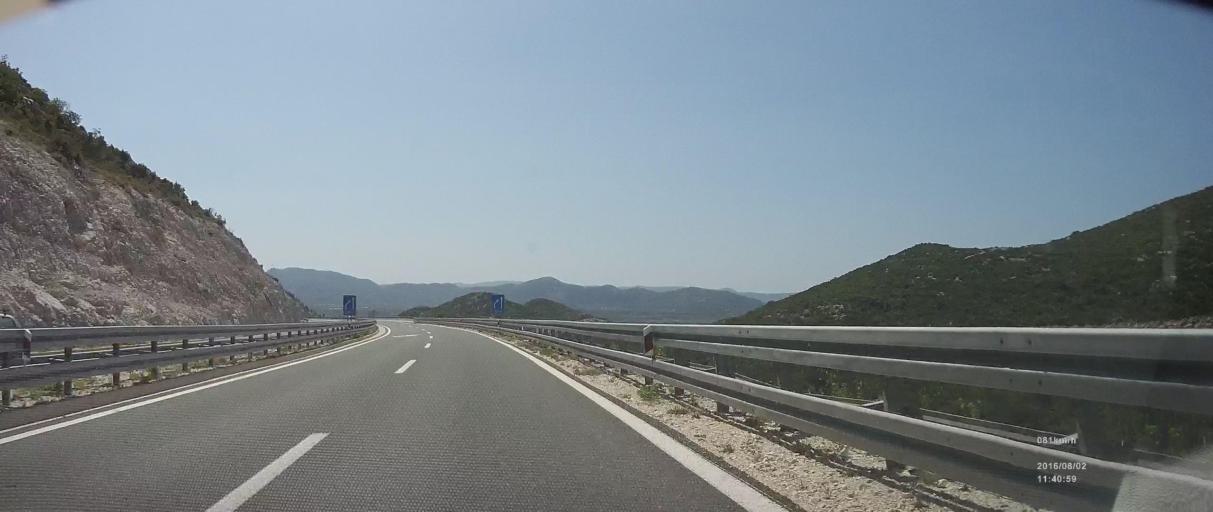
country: HR
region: Dubrovacko-Neretvanska
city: Komin
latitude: 43.0686
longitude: 17.4932
